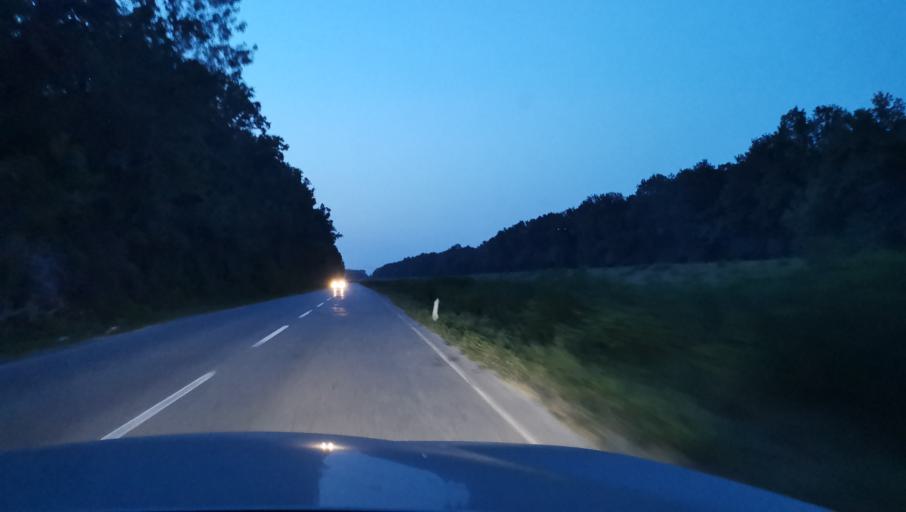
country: RS
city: Boljevci
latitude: 44.6959
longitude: 20.2000
